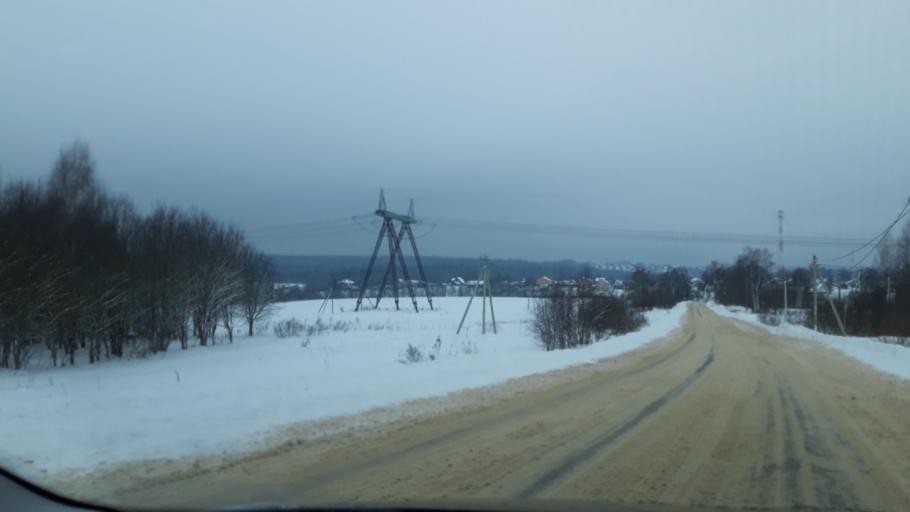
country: RU
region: Moskovskaya
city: Avtopoligon
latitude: 56.2590
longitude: 37.2402
